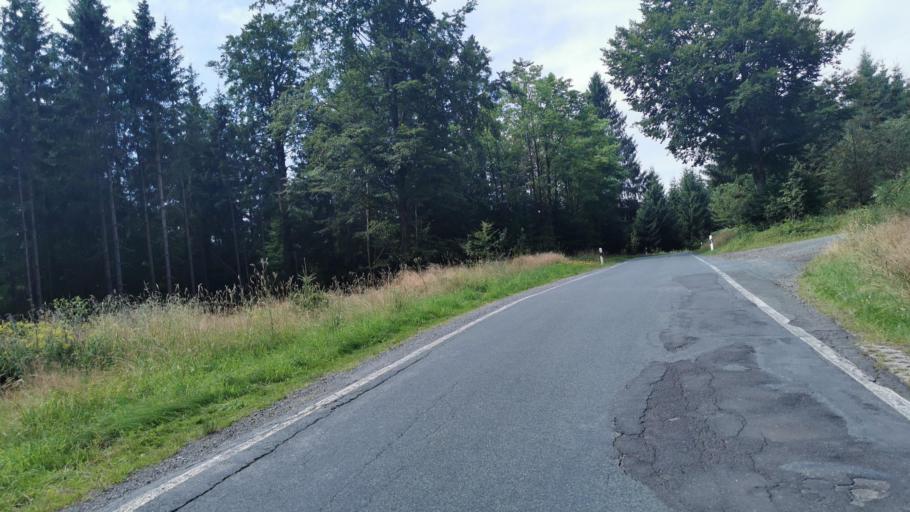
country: DE
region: Bavaria
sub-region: Upper Franconia
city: Tschirn
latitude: 50.3507
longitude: 11.4554
